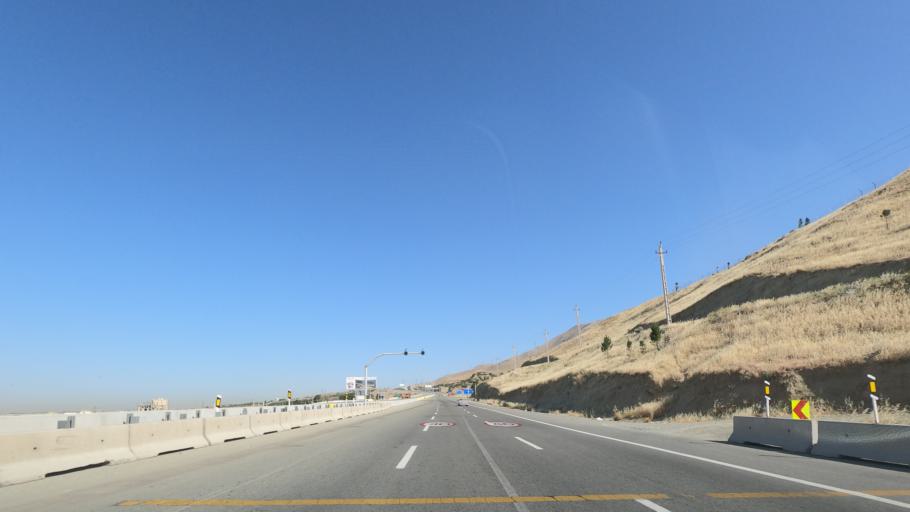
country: IR
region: Tehran
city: Shahr-e Qods
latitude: 35.7564
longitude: 51.0800
